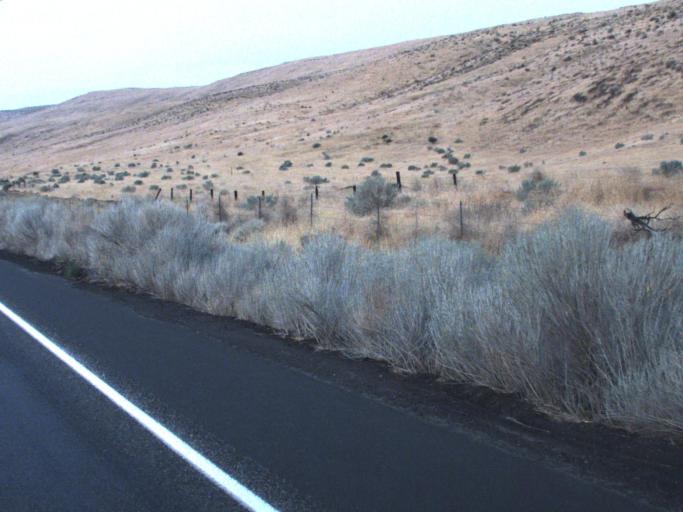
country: US
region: Washington
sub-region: Yakima County
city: Toppenish
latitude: 46.1766
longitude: -120.5011
